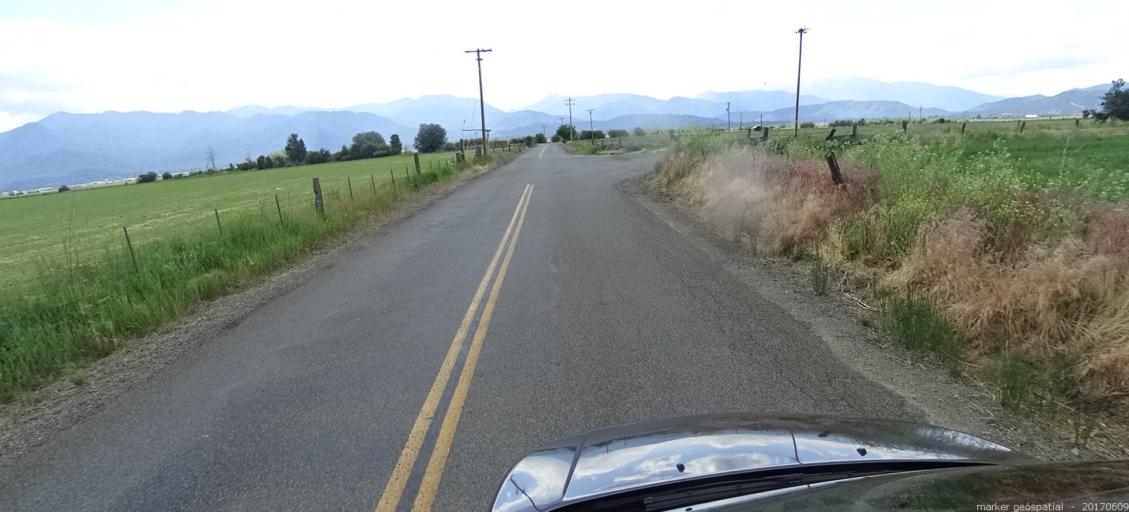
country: US
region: California
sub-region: Siskiyou County
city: Yreka
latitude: 41.5194
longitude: -122.8575
